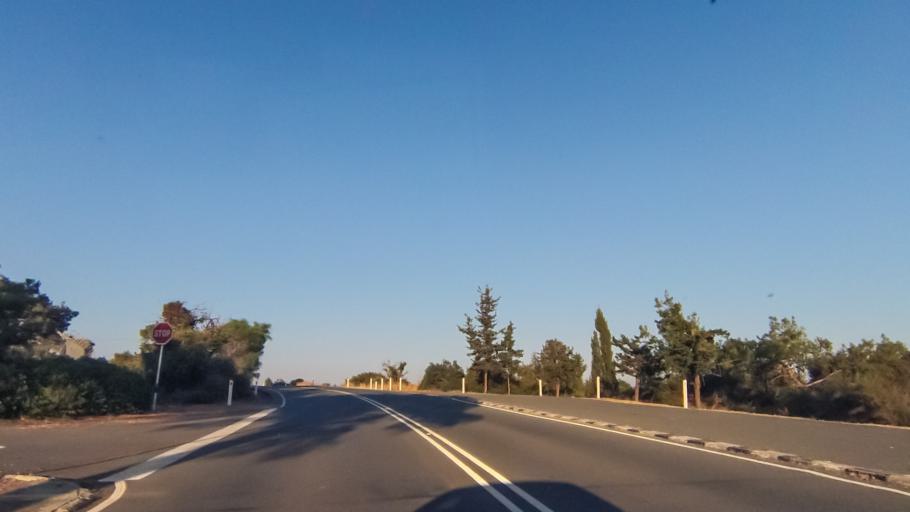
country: CY
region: Limassol
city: Sotira
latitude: 34.6742
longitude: 32.8464
